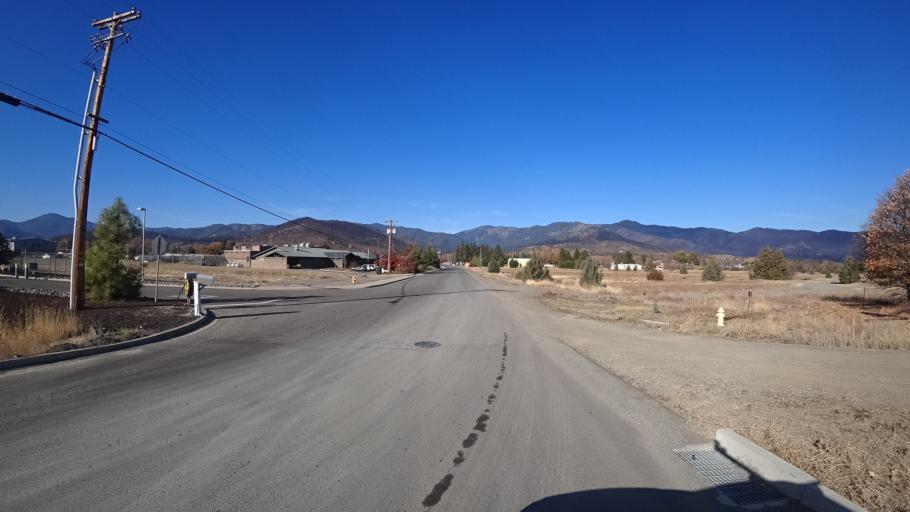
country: US
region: California
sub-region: Siskiyou County
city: Yreka
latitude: 41.7085
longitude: -122.6334
